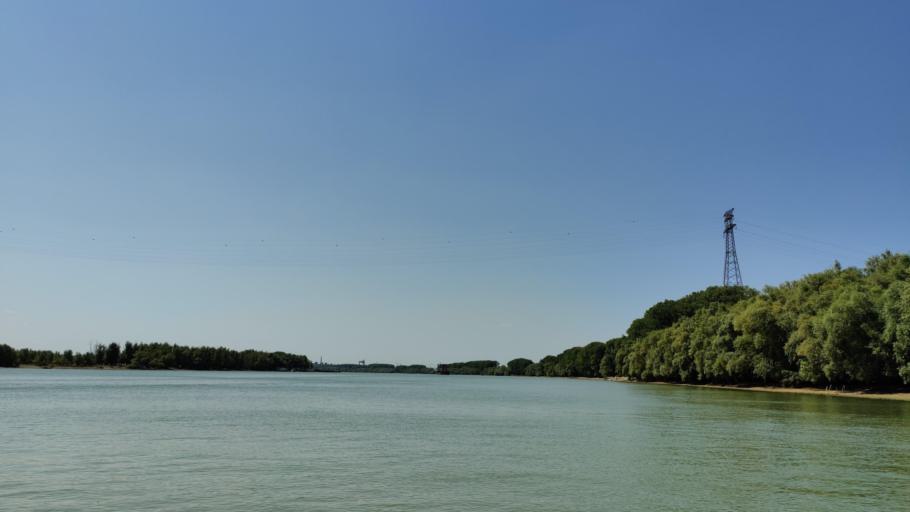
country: RO
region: Tulcea
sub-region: Municipiul Tulcea
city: Tulcea
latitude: 45.2039
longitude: 28.8497
